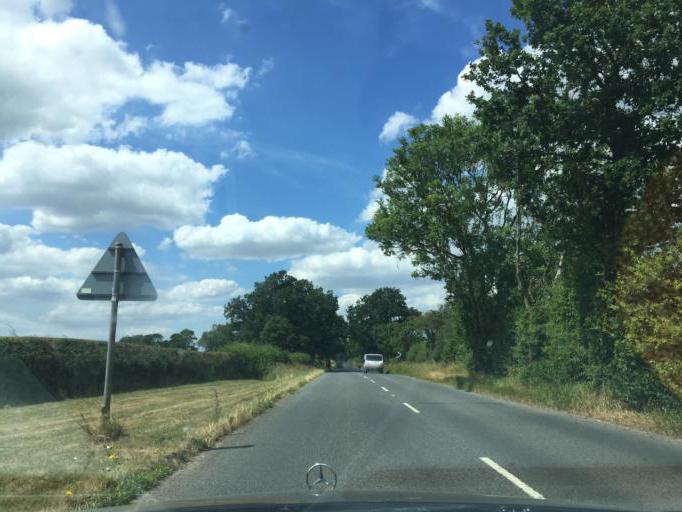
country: GB
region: England
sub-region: Leicestershire
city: Hinckley
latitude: 52.4905
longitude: -1.3486
